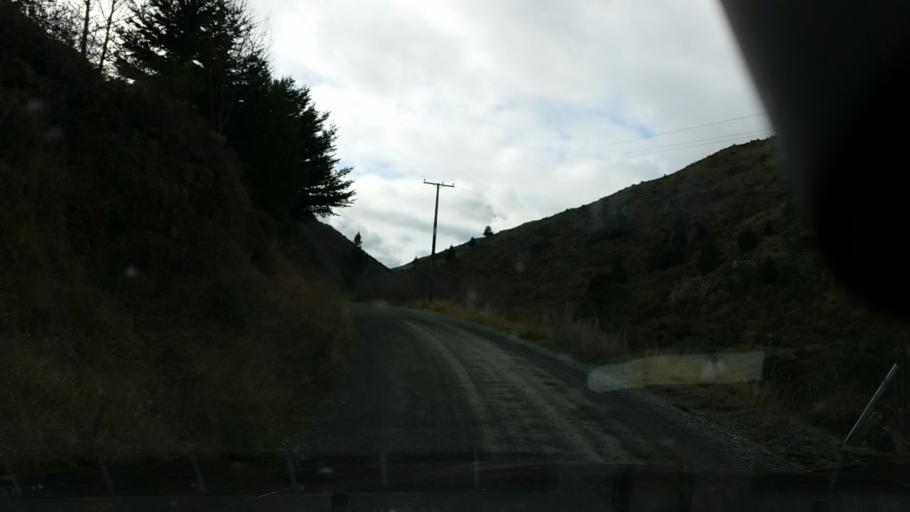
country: NZ
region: Tasman
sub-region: Tasman District
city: Richmond
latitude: -41.7203
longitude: 173.4718
